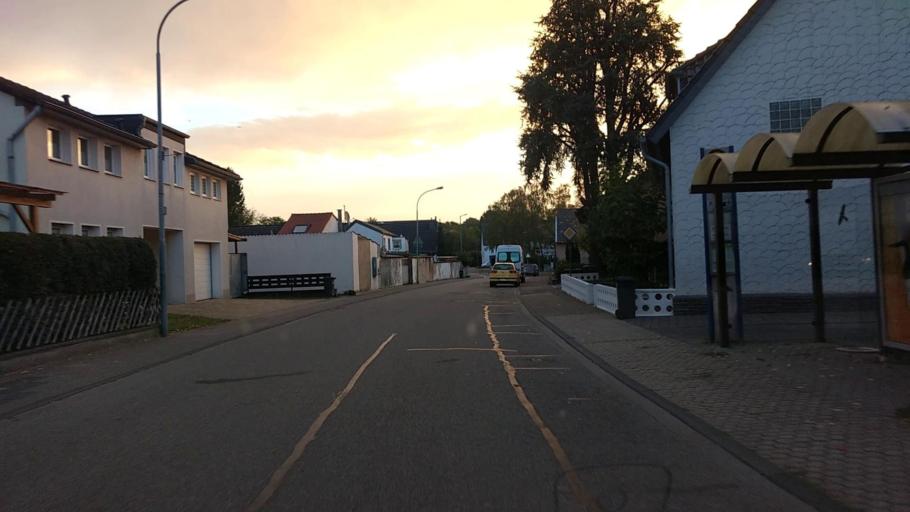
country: DE
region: North Rhine-Westphalia
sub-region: Regierungsbezirk Koln
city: Bergheim
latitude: 50.9266
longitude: 6.6594
